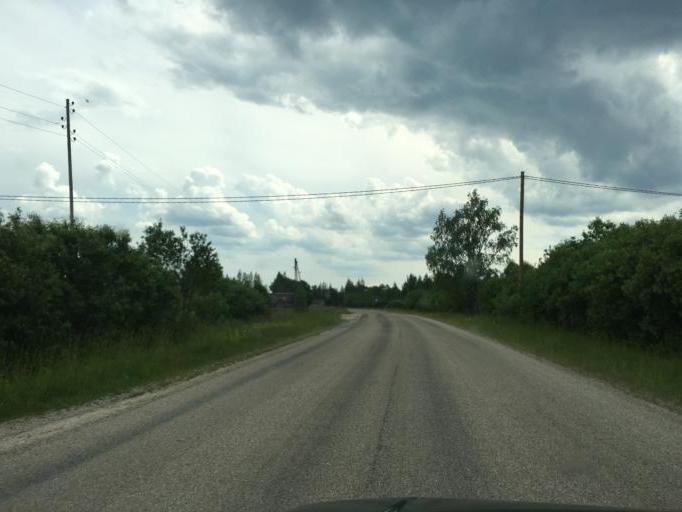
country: LV
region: Rugaju
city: Rugaji
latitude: 56.9094
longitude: 27.0652
